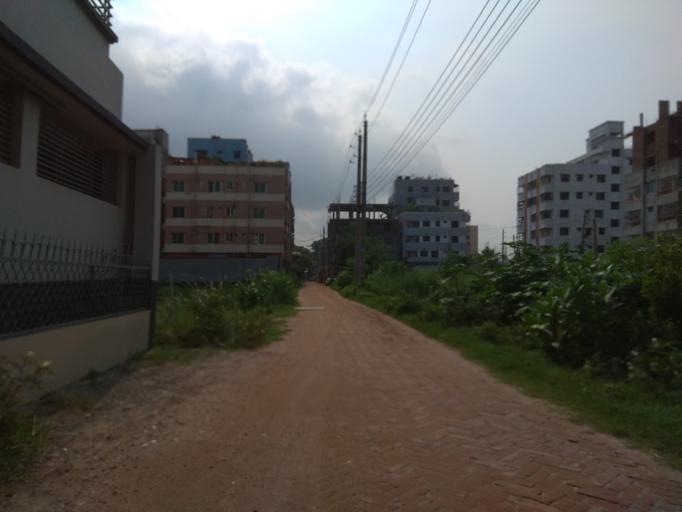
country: BD
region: Dhaka
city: Tungi
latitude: 23.8315
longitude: 90.3540
